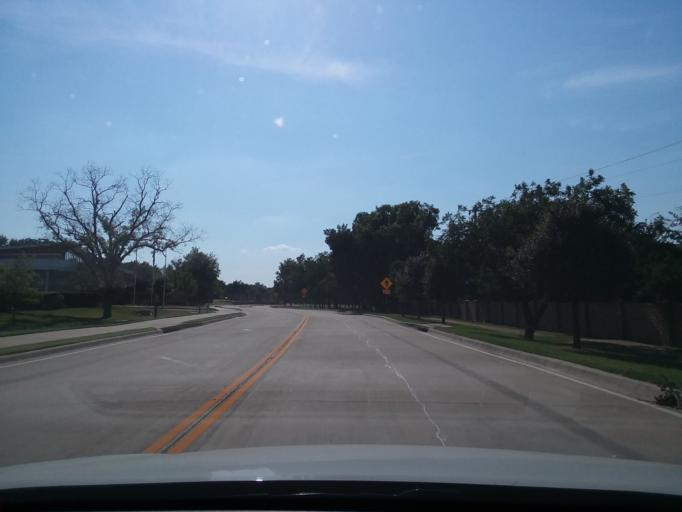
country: US
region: Texas
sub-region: Denton County
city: Flower Mound
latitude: 33.0477
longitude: -97.0711
